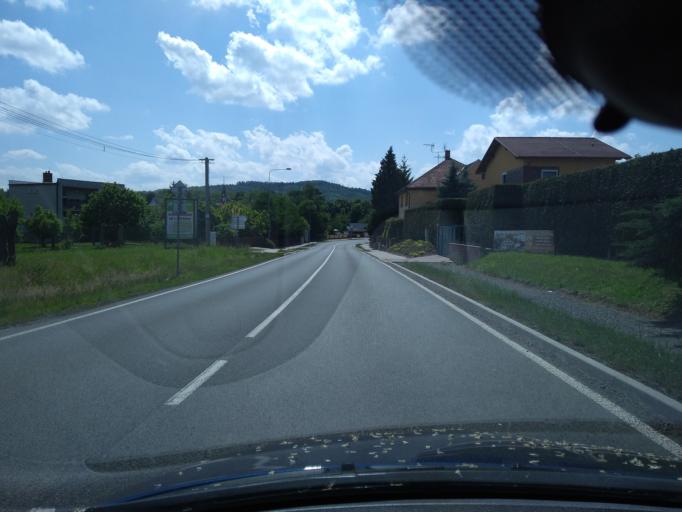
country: CZ
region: Plzensky
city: Prestice
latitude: 49.5496
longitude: 13.3155
